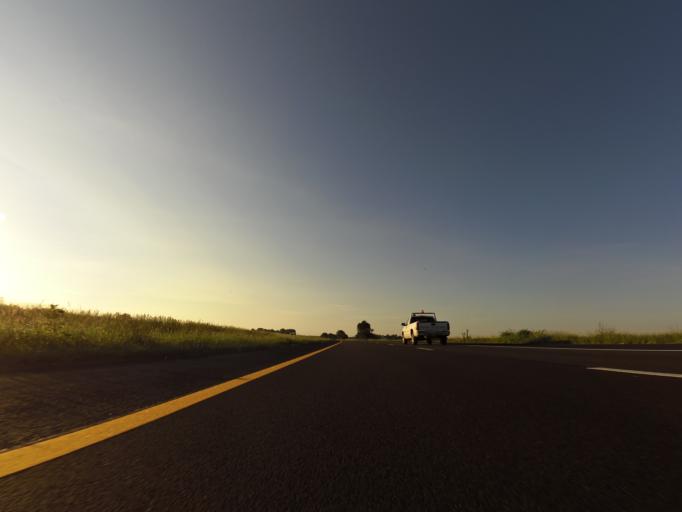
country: US
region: Kansas
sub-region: Sedgwick County
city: Colwich
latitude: 37.8611
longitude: -97.6173
